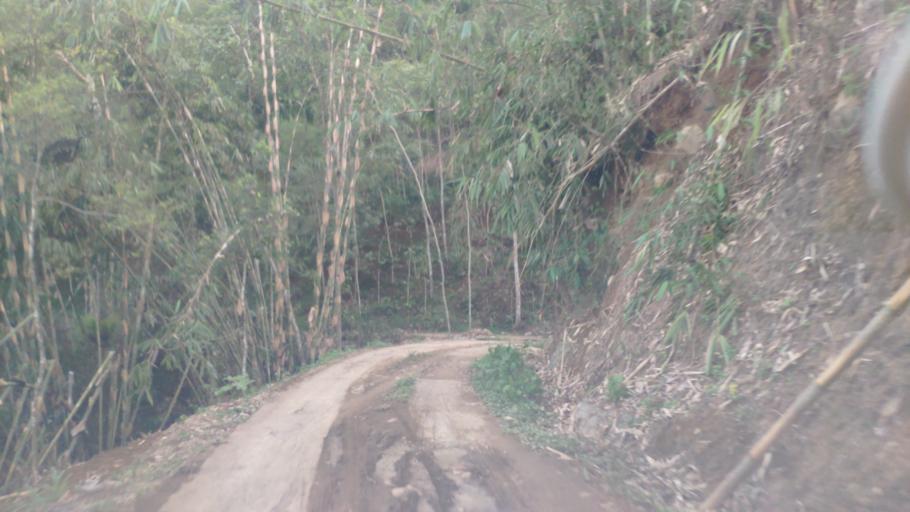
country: ID
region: Central Java
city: Buaran
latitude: -7.2612
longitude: 109.5728
